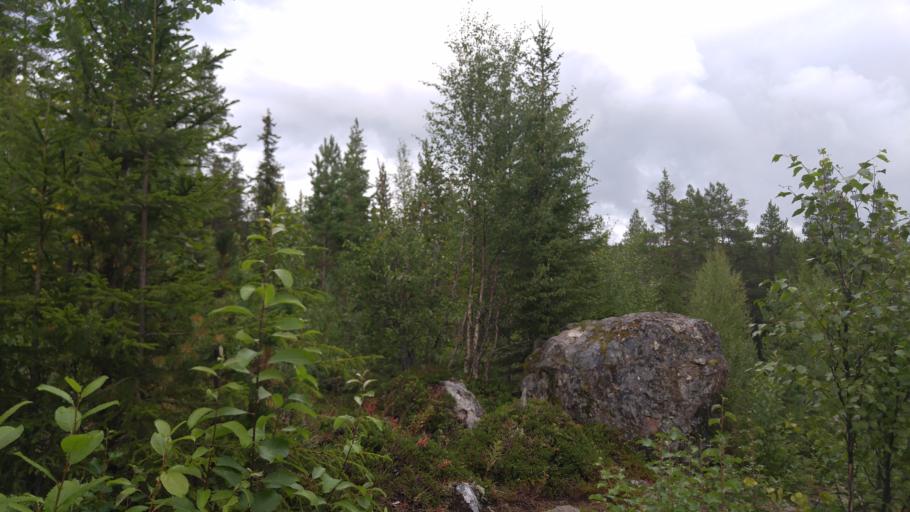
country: NO
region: Buskerud
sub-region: Gol
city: Gol
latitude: 60.6346
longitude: 9.0085
